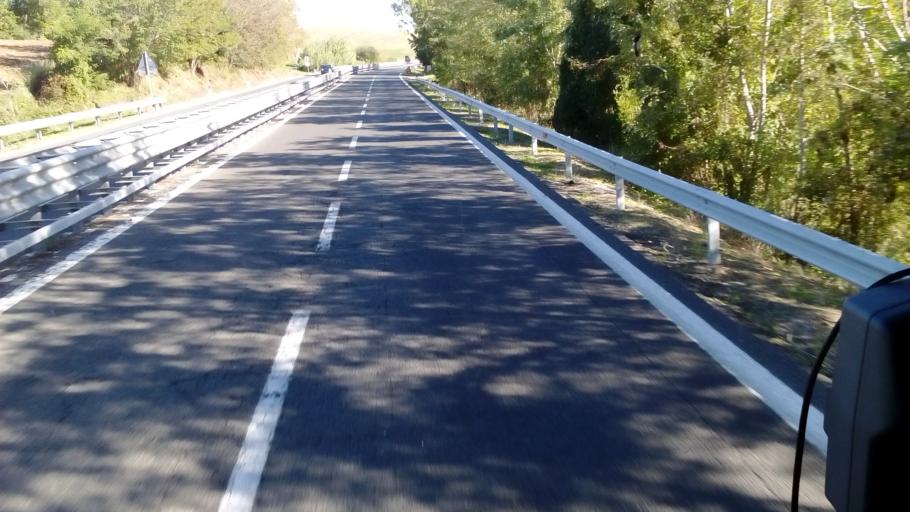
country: IT
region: Latium
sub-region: Provincia di Viterbo
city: Montalto di Castro
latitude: 42.3211
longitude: 11.6449
